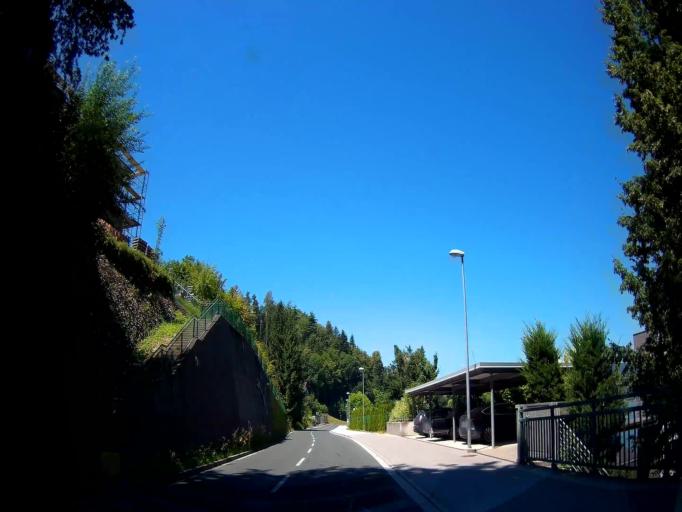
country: AT
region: Carinthia
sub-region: Politischer Bezirk Klagenfurt Land
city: Maria Worth
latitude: 46.6122
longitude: 14.1722
